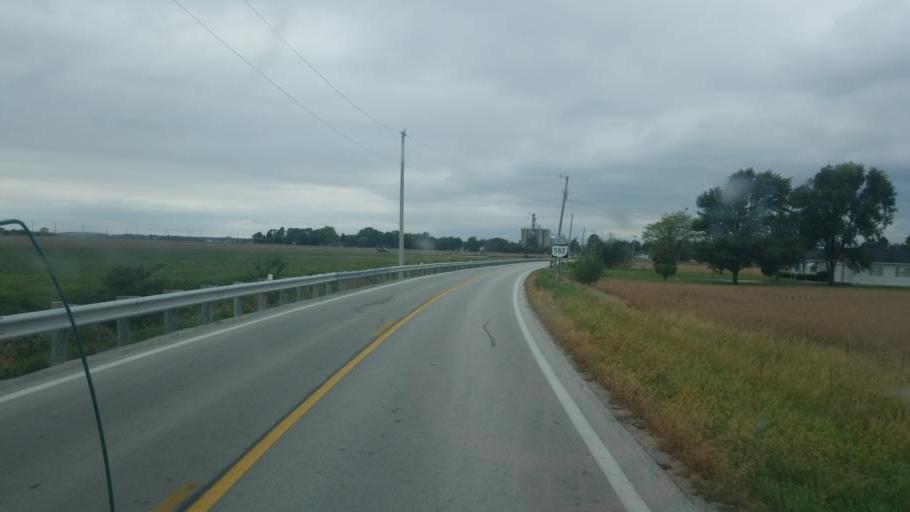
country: US
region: Ohio
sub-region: Wood County
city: Haskins
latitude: 41.4569
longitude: -83.7024
